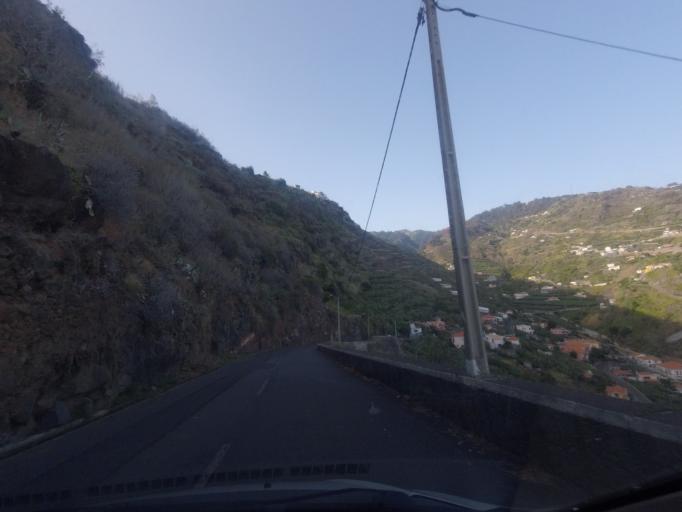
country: PT
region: Madeira
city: Ponta do Sol
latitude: 32.6793
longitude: -17.0799
